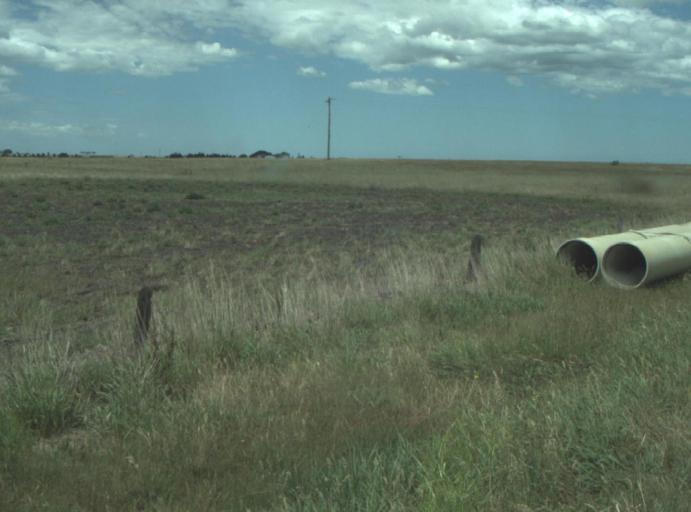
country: AU
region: Victoria
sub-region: Wyndham
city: Little River
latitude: -37.8956
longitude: 144.4641
